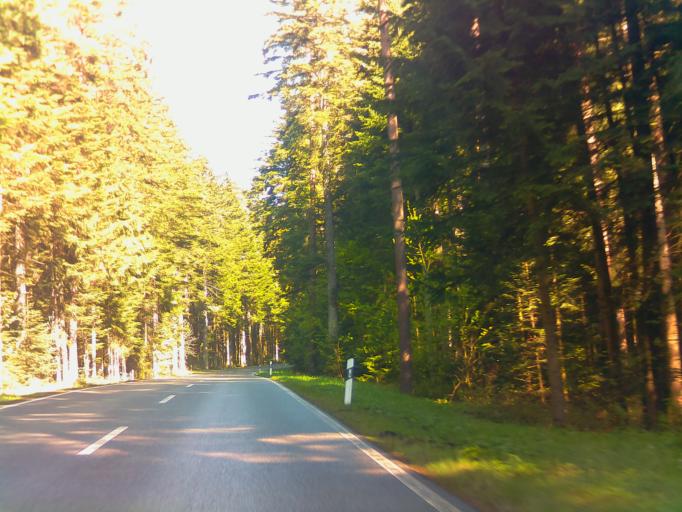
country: DE
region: Baden-Wuerttemberg
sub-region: Karlsruhe Region
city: Neuweiler
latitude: 48.6555
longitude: 8.5673
